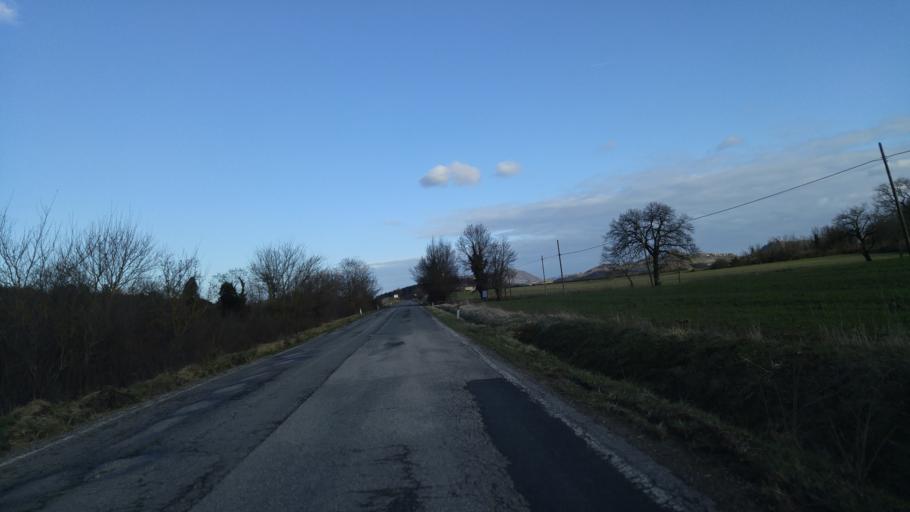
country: IT
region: The Marches
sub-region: Provincia di Pesaro e Urbino
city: Cagli
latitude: 43.5399
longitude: 12.6848
